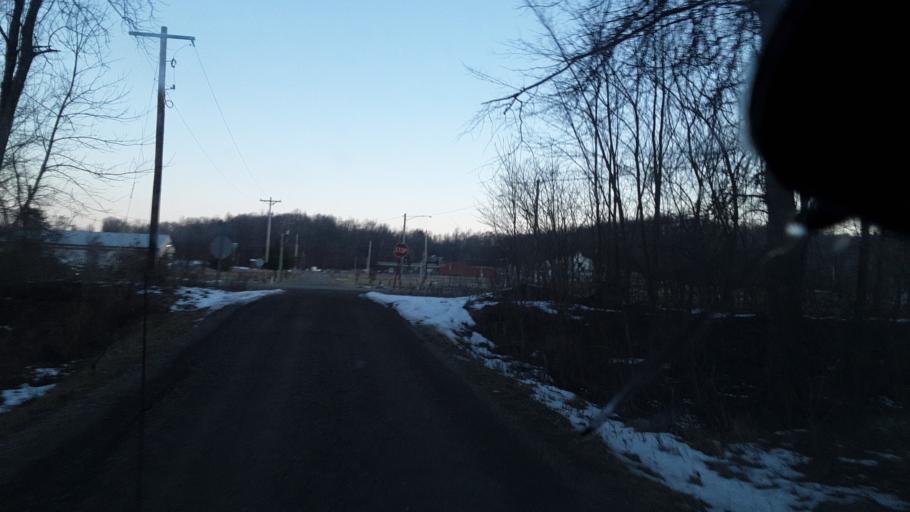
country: US
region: Ohio
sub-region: Perry County
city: Somerset
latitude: 39.7217
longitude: -82.3092
